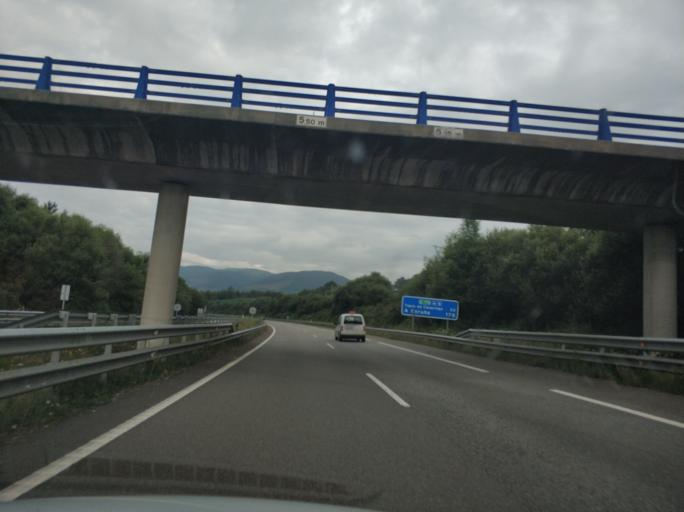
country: ES
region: Asturias
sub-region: Province of Asturias
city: Navia
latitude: 43.5330
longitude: -6.7008
